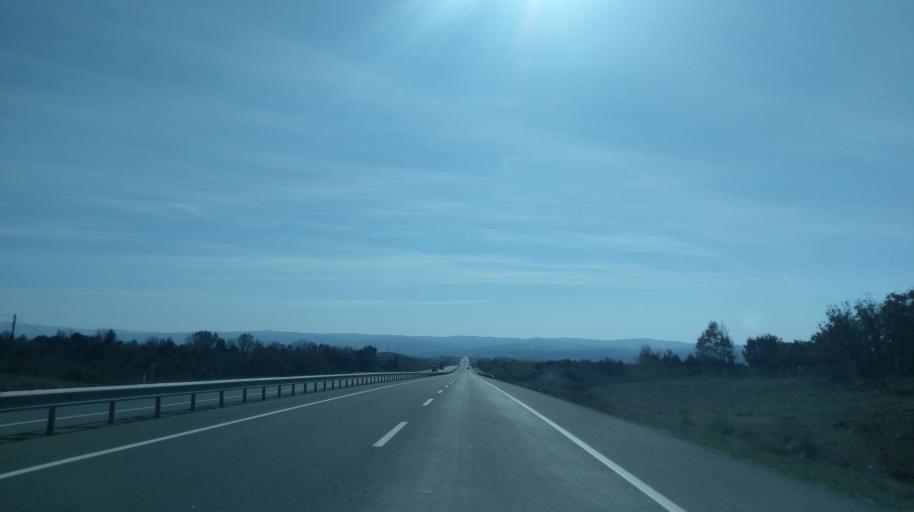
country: TR
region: Edirne
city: Kesan
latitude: 40.8037
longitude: 26.6636
